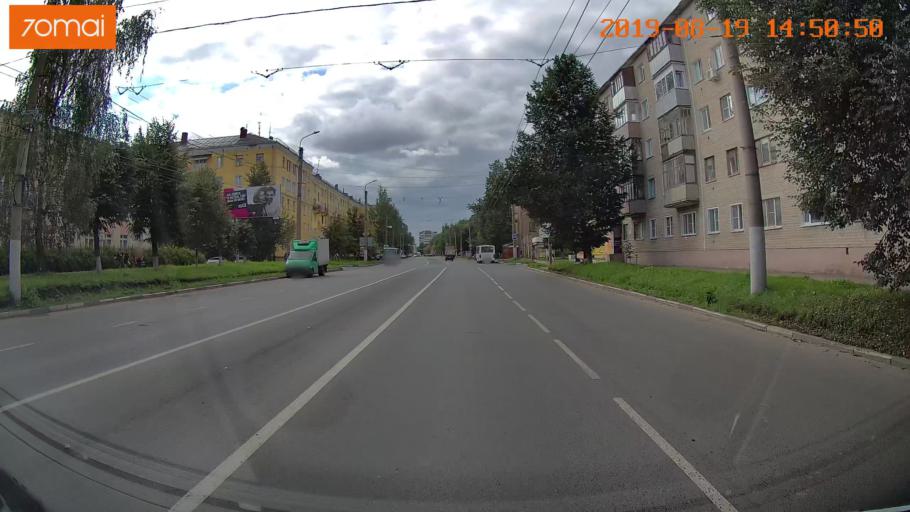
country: RU
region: Ivanovo
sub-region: Gorod Ivanovo
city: Ivanovo
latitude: 56.9944
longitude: 41.0077
